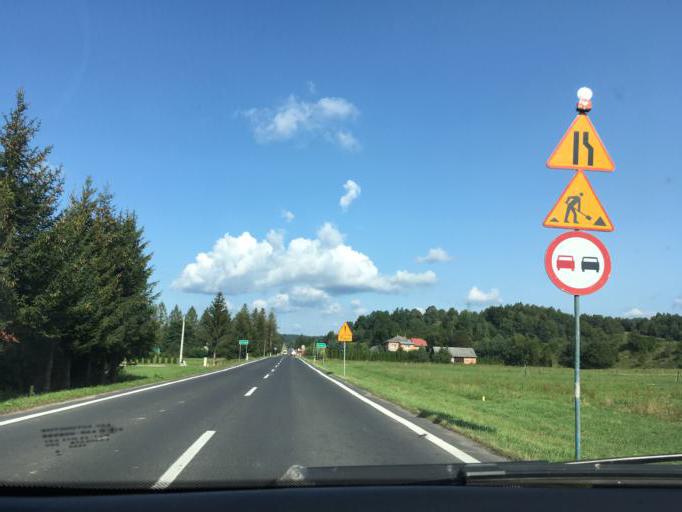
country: PL
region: Subcarpathian Voivodeship
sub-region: Powiat leski
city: Olszanica
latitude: 49.4672
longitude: 22.4644
